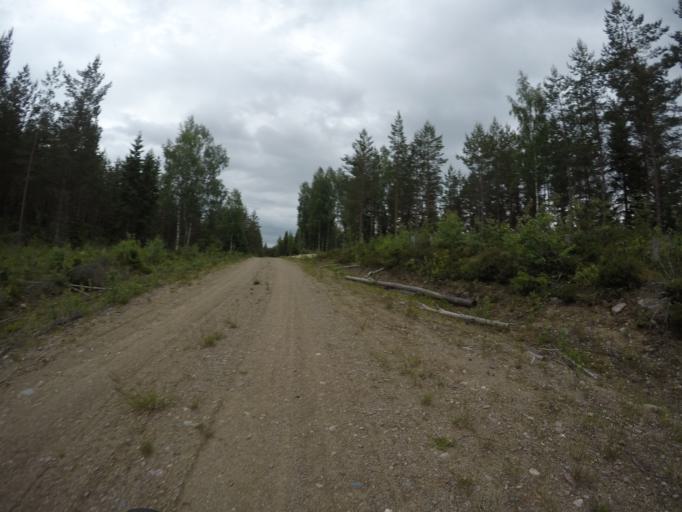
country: SE
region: Dalarna
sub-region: Ludvika Kommun
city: Abborrberget
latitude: 60.0649
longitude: 14.5596
